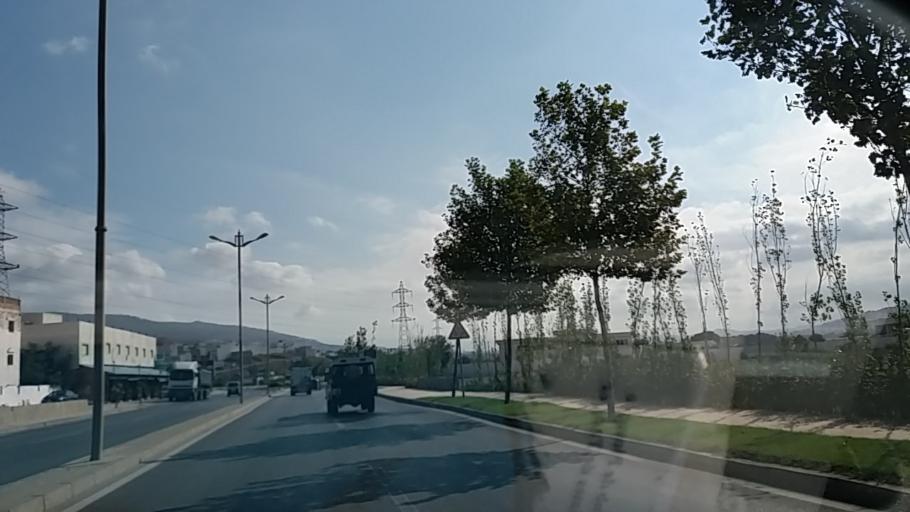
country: MA
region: Tanger-Tetouan
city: Tetouan
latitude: 35.5643
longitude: -5.4234
